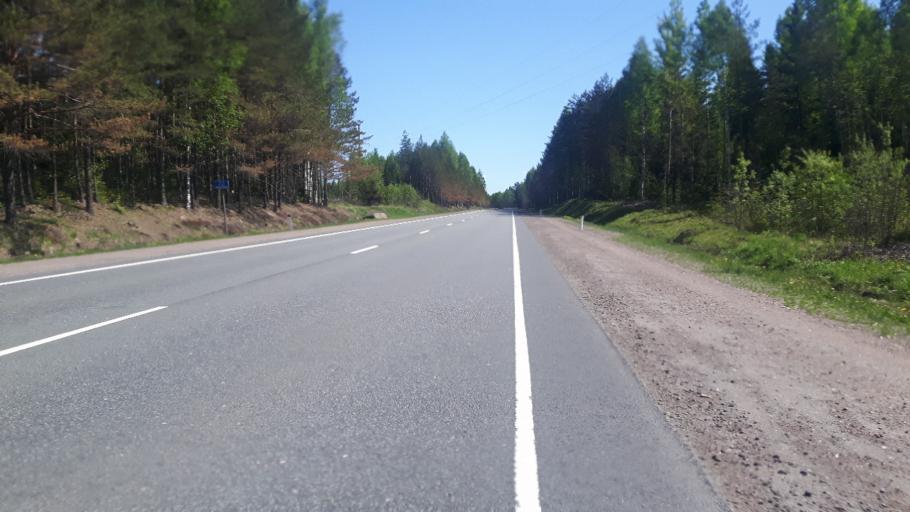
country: FI
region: South Karelia
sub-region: Lappeenranta
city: Ylaemaa
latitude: 60.6263
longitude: 28.2249
